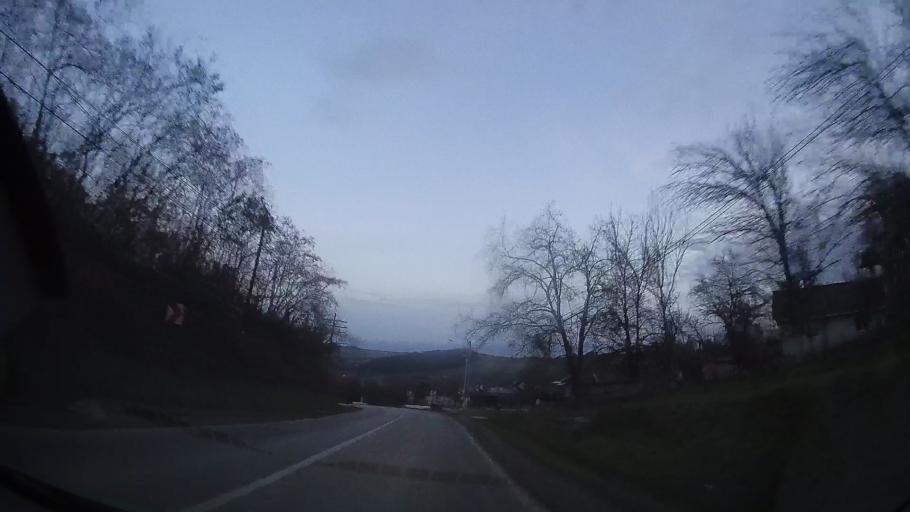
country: RO
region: Cluj
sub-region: Comuna Mociu
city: Mociu
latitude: 46.7973
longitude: 24.0174
